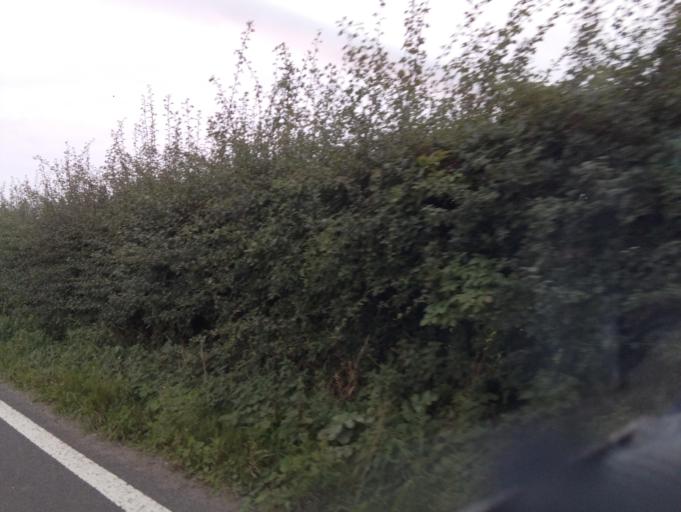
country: GB
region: England
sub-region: Derbyshire
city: Bradley
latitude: 53.0189
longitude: -1.6583
